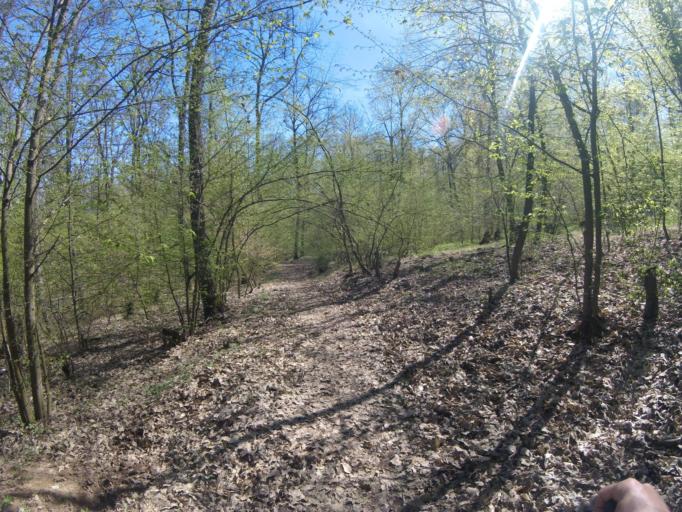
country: HU
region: Borsod-Abauj-Zemplen
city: Szendro
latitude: 48.4078
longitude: 20.7641
